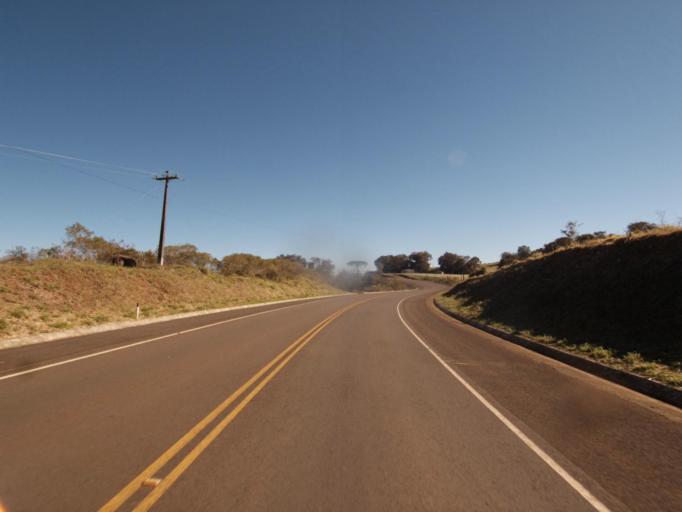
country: AR
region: Misiones
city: Bernardo de Irigoyen
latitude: -26.6710
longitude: -53.5800
